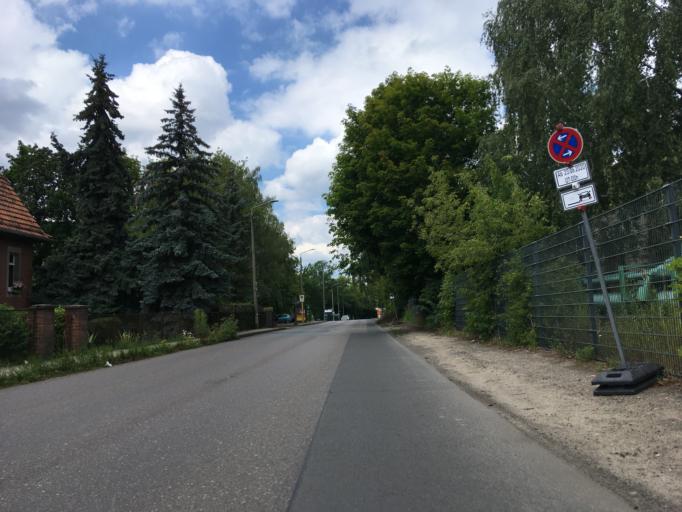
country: DE
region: Berlin
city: Buch
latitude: 52.6351
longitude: 13.5087
